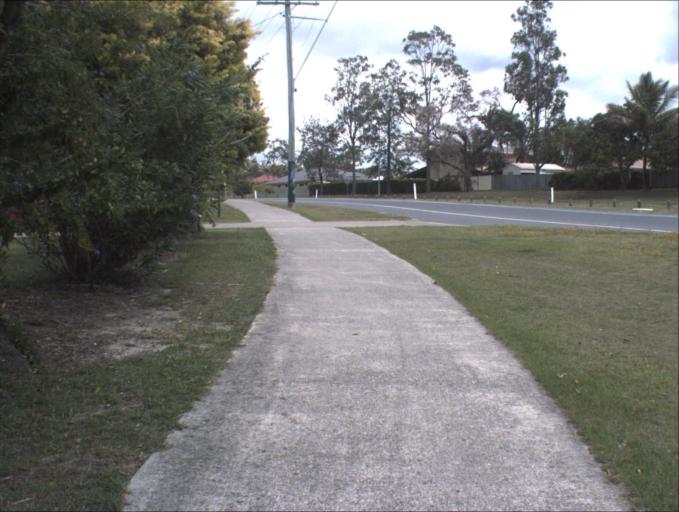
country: AU
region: Queensland
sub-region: Logan
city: Logan Reserve
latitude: -27.6795
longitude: 153.0615
